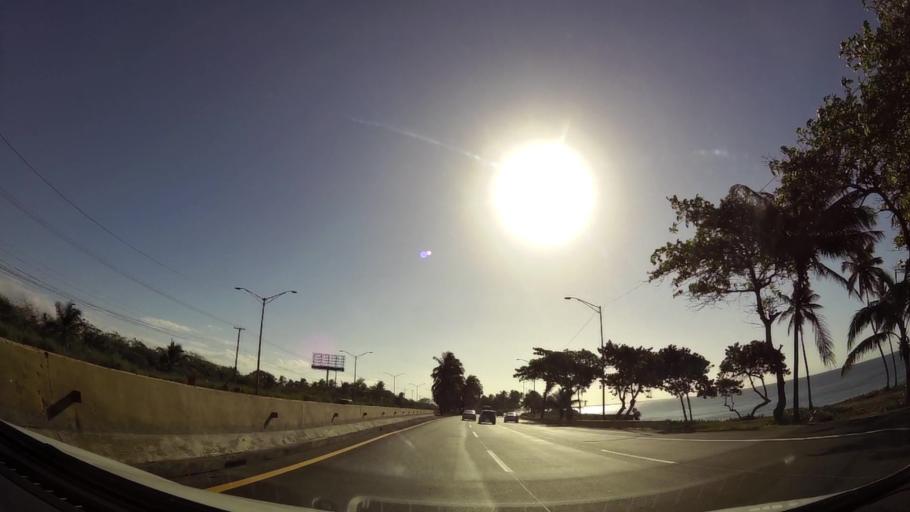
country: DO
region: Santo Domingo
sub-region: Santo Domingo
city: Santo Domingo Este
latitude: 18.4644
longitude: -69.7586
